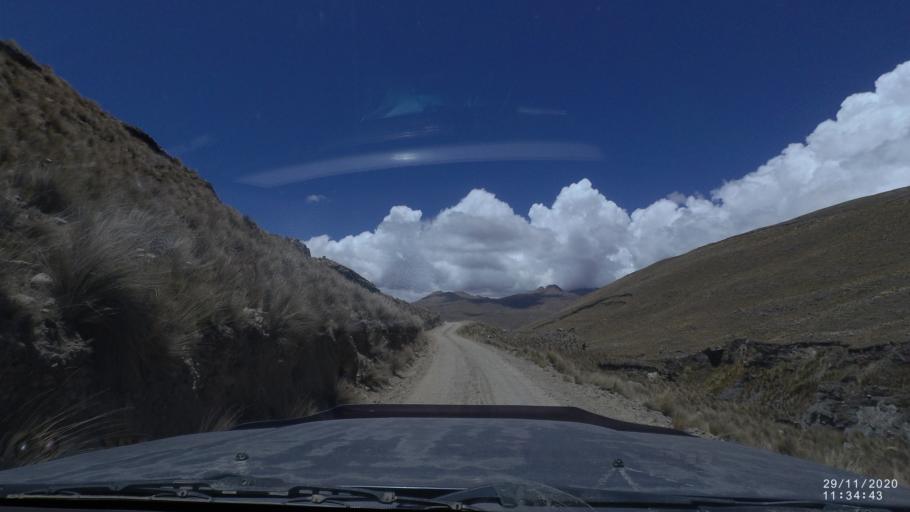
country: BO
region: Cochabamba
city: Cochabamba
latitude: -17.1894
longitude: -66.2219
